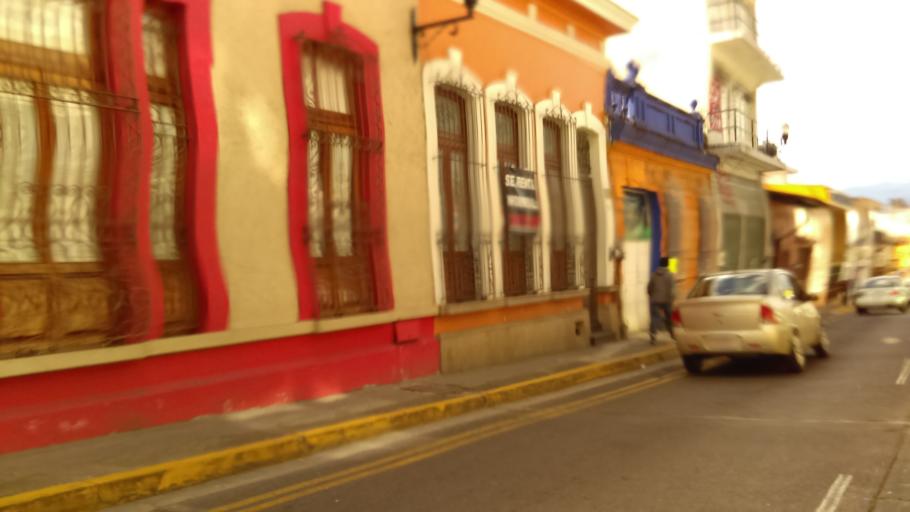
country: MX
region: Veracruz
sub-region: Xalapa
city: Xalapa de Enriquez
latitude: 19.5267
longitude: -96.9252
